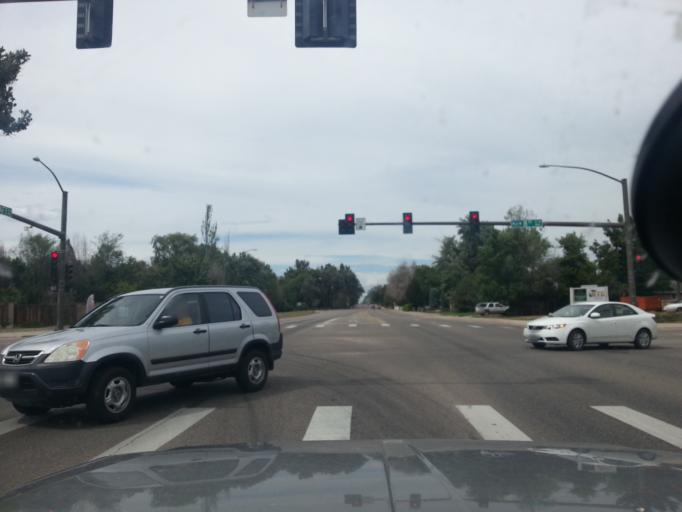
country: US
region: Colorado
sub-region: Larimer County
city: Loveland
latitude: 40.3998
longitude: -105.0970
